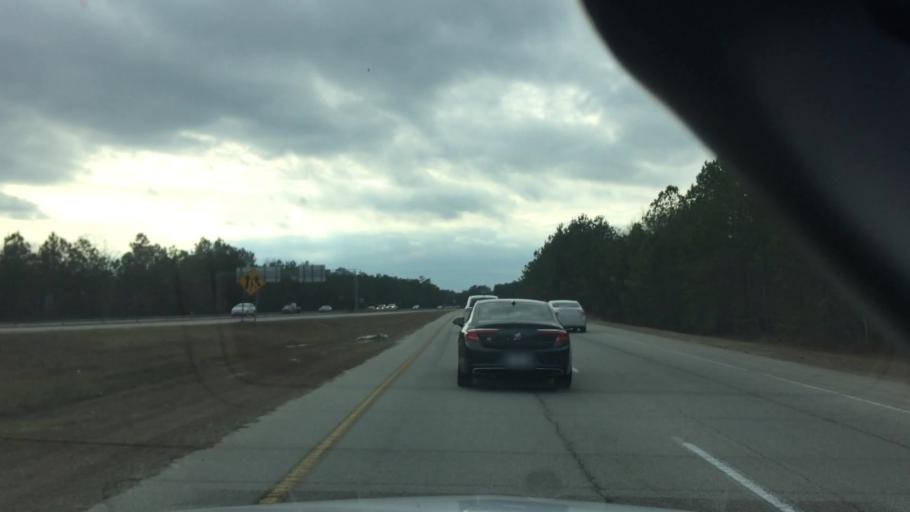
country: US
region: South Carolina
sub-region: Horry County
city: North Myrtle Beach
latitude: 33.8742
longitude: -78.6844
